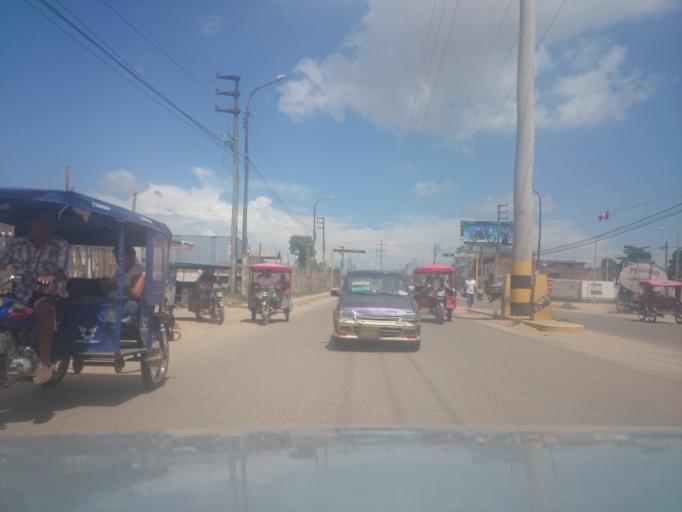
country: PE
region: Ucayali
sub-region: Provincia de Coronel Portillo
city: Pucallpa
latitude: -8.3858
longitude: -74.5541
